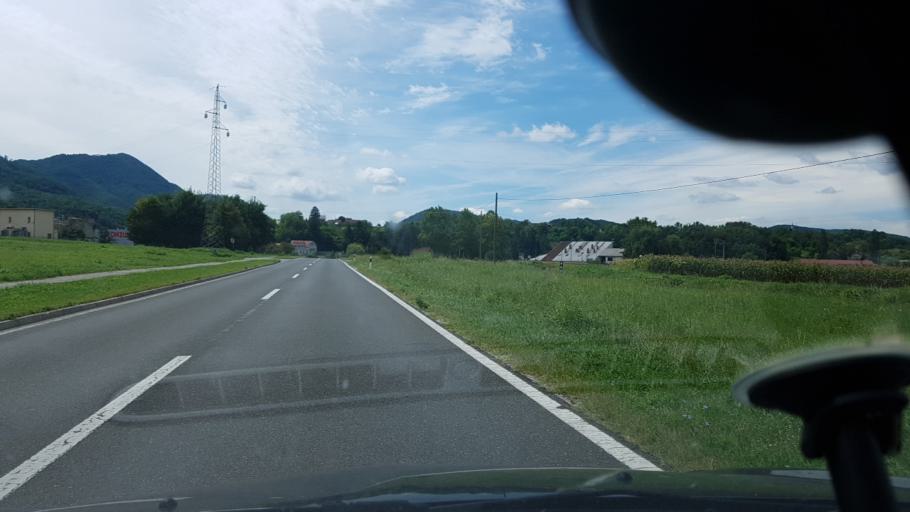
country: HR
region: Varazdinska
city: Lepoglava
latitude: 46.2121
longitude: 16.0409
